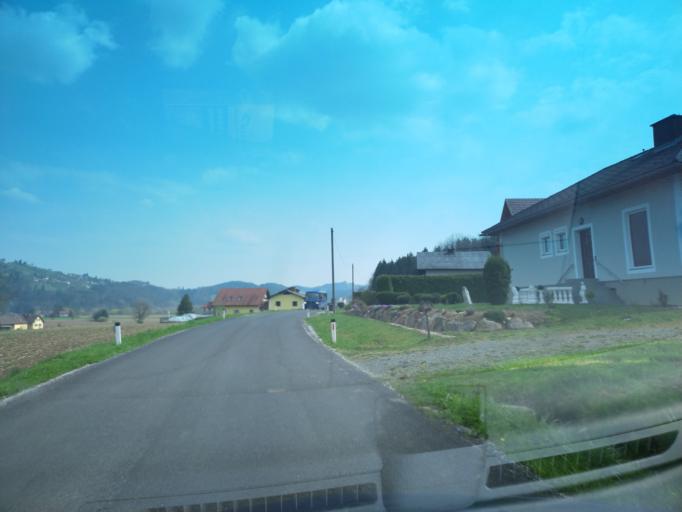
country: AT
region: Styria
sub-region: Politischer Bezirk Leibnitz
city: Kitzeck im Sausal
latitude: 46.7473
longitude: 15.4219
